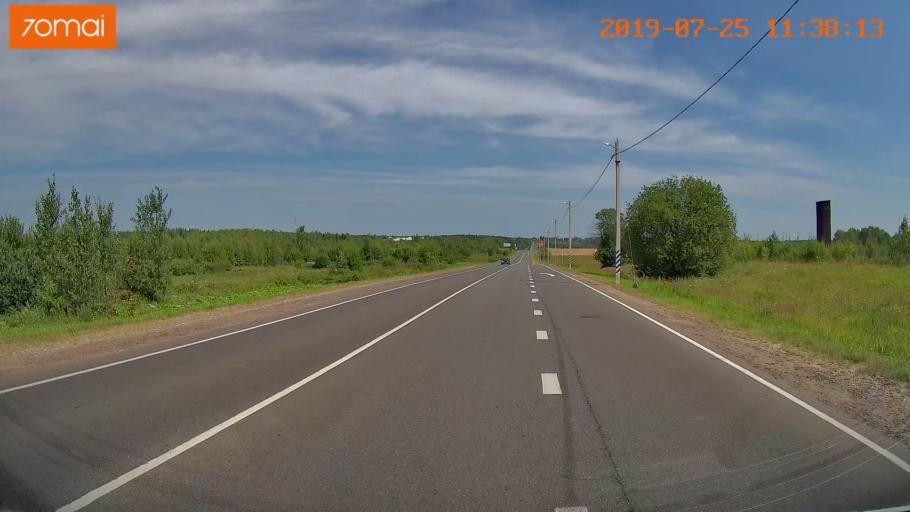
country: RU
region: Ivanovo
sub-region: Privolzhskiy Rayon
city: Ples
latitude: 57.4397
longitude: 41.4800
